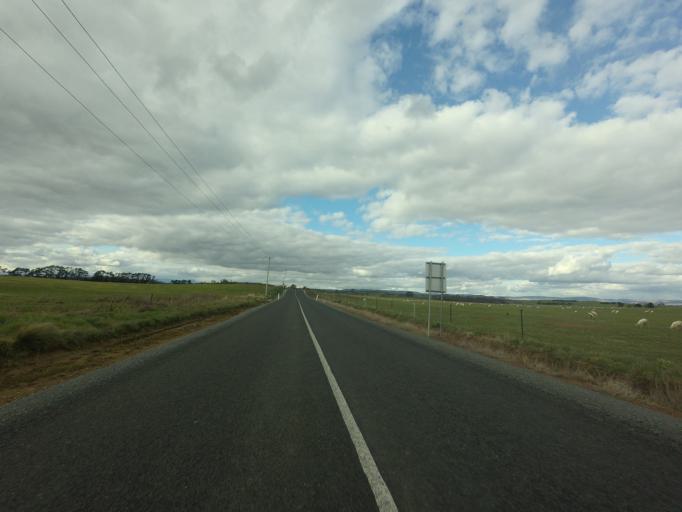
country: AU
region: Tasmania
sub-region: Northern Midlands
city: Evandale
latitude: -41.9119
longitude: 147.3787
